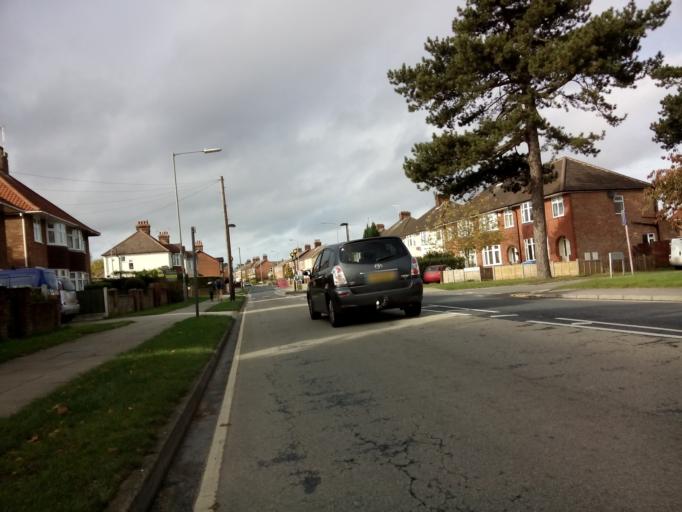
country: GB
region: England
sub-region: Suffolk
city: Ipswich
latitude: 52.0451
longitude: 1.1888
